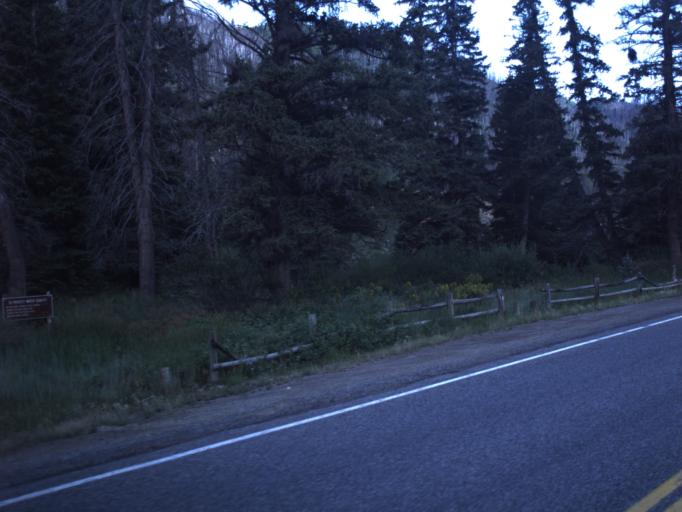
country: US
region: Utah
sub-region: Sanpete County
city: Fairview
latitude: 39.5525
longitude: -111.1703
